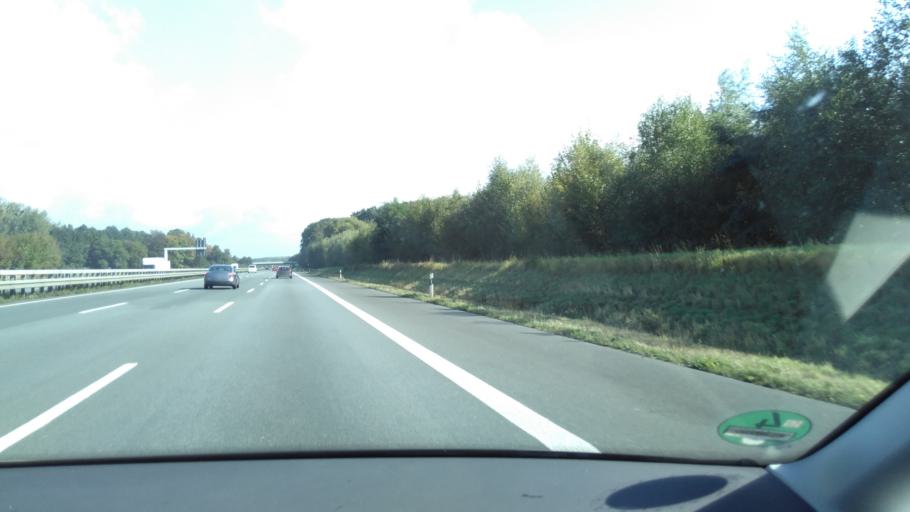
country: DE
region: North Rhine-Westphalia
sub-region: Regierungsbezirk Arnsberg
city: Welver
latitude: 51.6385
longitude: 7.8945
